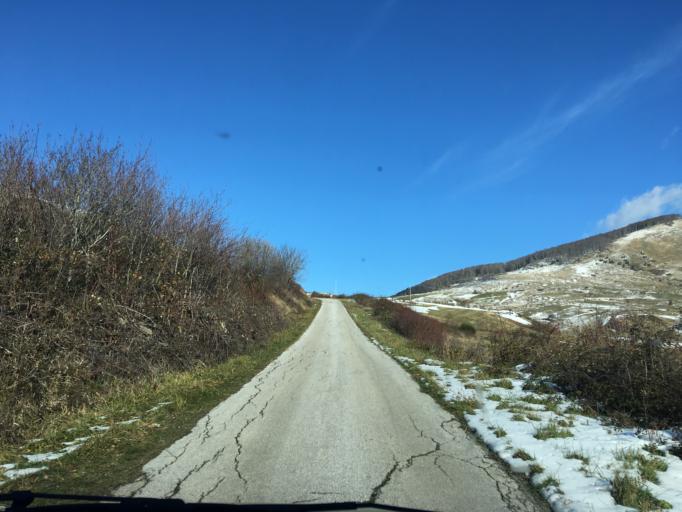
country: IT
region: Molise
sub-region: Provincia di Isernia
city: Agnone
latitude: 41.8520
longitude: 14.3555
